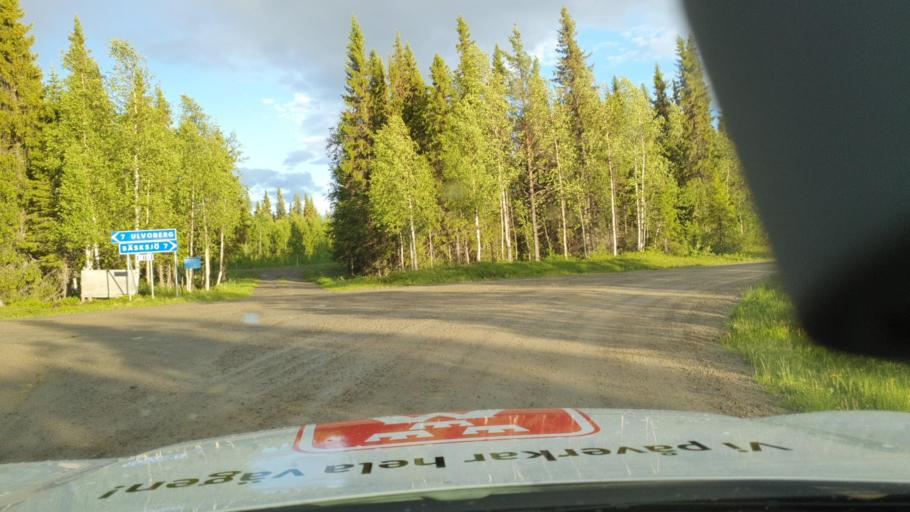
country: SE
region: Vaesterbotten
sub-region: Storumans Kommun
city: Storuman
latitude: 64.7507
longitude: 17.0867
